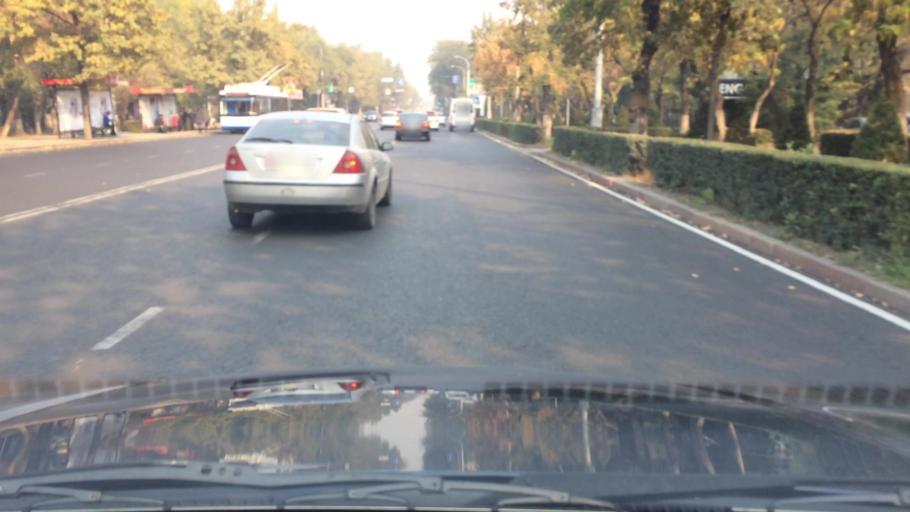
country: KG
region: Chuy
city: Bishkek
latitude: 42.8473
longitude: 74.5863
